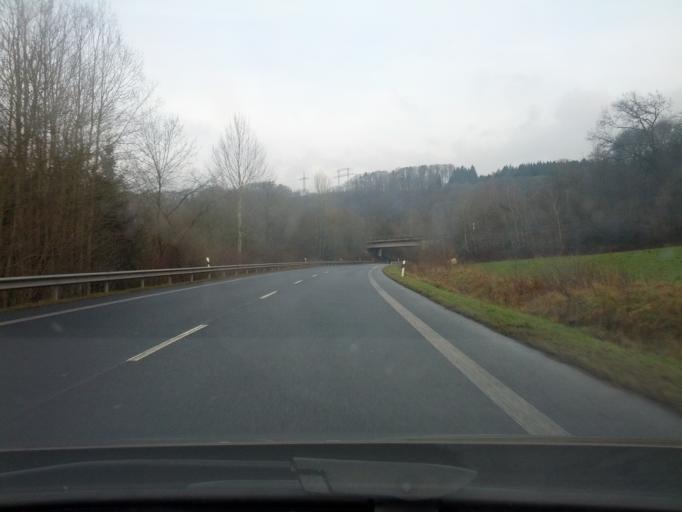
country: DE
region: Lower Saxony
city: Scheden
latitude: 51.3965
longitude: 9.7273
